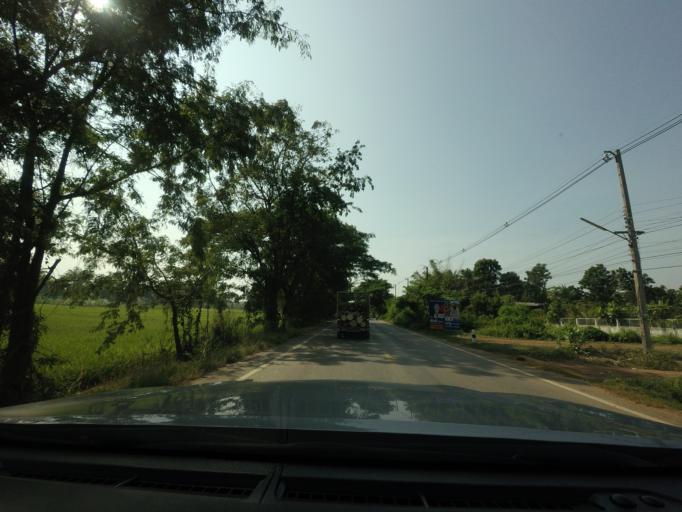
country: TH
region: Sukhothai
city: Kong Krailat
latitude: 16.8545
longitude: 99.9408
